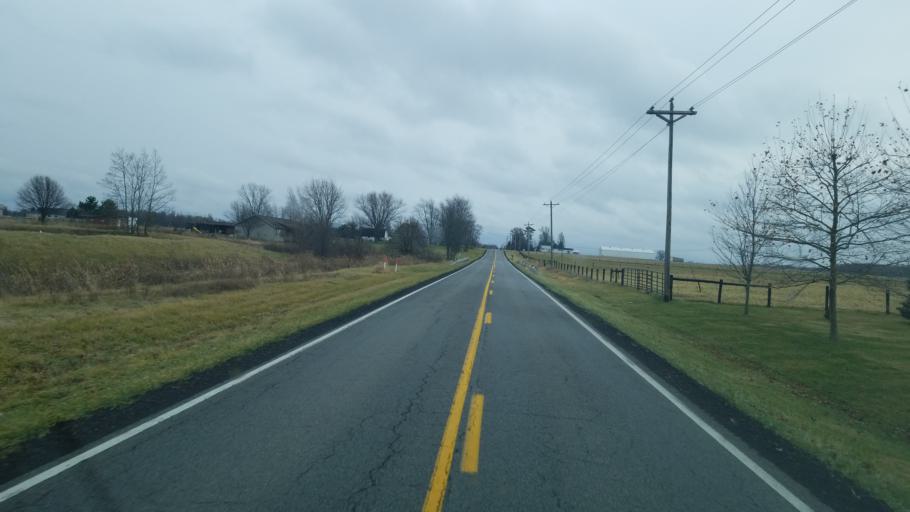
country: US
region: Ohio
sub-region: Union County
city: Marysville
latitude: 40.3089
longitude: -83.3527
